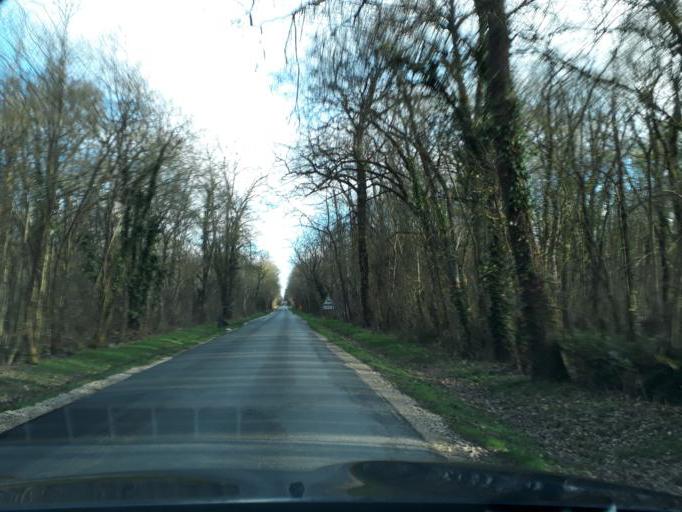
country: FR
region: Centre
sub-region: Departement du Loiret
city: Mareau-aux-Pres
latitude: 47.8175
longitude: 1.8069
